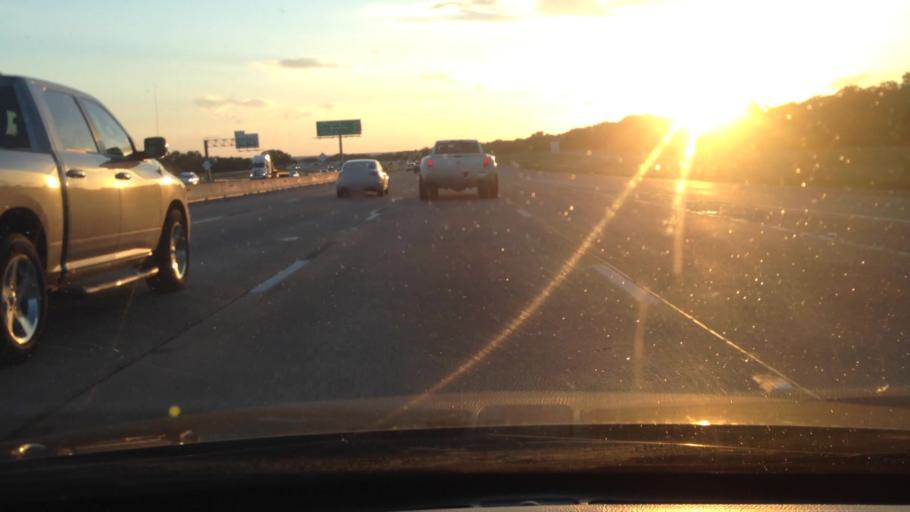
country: US
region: Texas
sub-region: Tarrant County
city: Lake Worth
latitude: 32.7979
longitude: -97.4443
